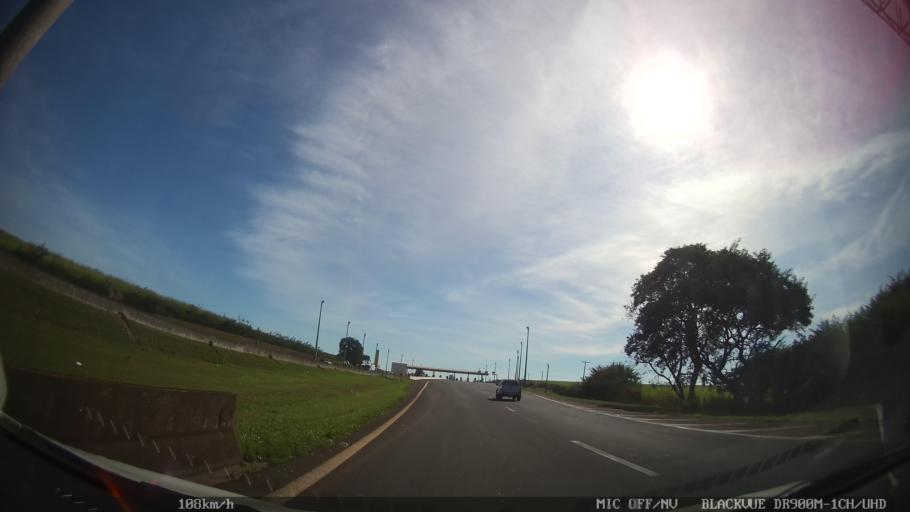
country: BR
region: Sao Paulo
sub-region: Leme
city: Leme
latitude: -22.2528
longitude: -47.3898
